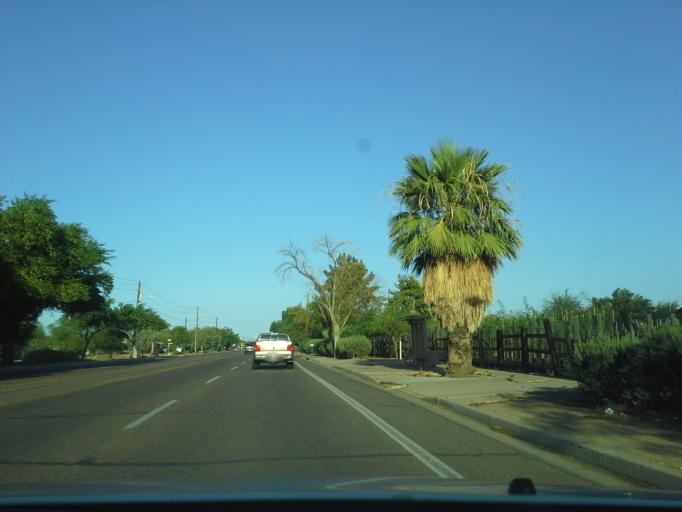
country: US
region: Arizona
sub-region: Maricopa County
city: Guadalupe
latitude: 33.3925
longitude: -112.0090
